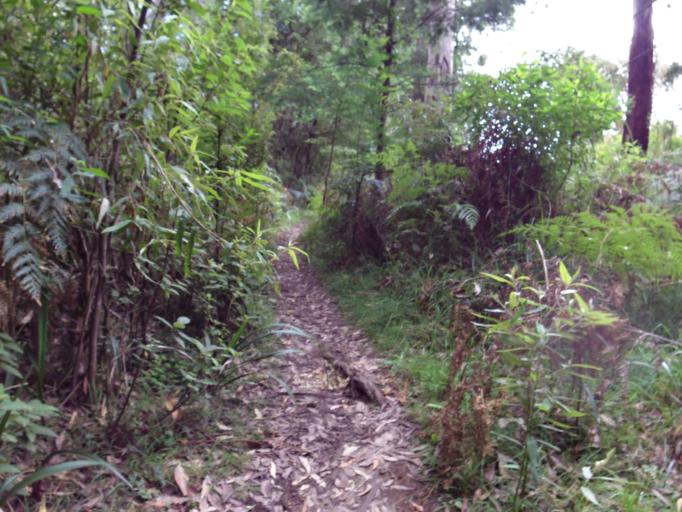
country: AU
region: Victoria
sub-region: Yarra Ranges
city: Kallista
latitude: -37.8791
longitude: 145.3584
